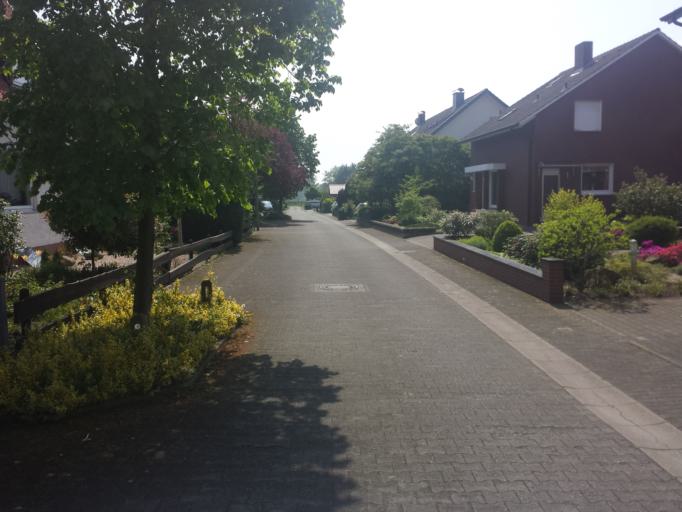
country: DE
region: North Rhine-Westphalia
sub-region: Regierungsbezirk Detmold
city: Guetersloh
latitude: 51.9063
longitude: 8.4274
